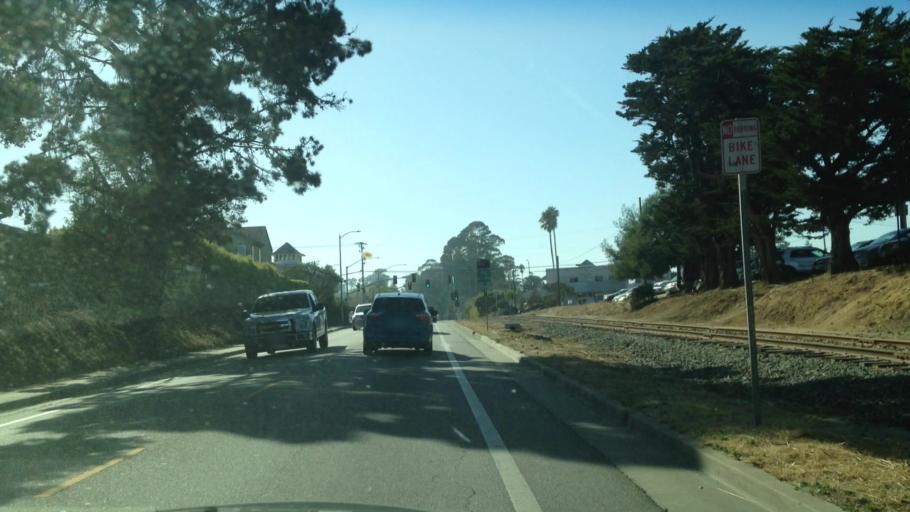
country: US
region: California
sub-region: Santa Cruz County
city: Twin Lakes
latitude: 36.9677
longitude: -122.0062
